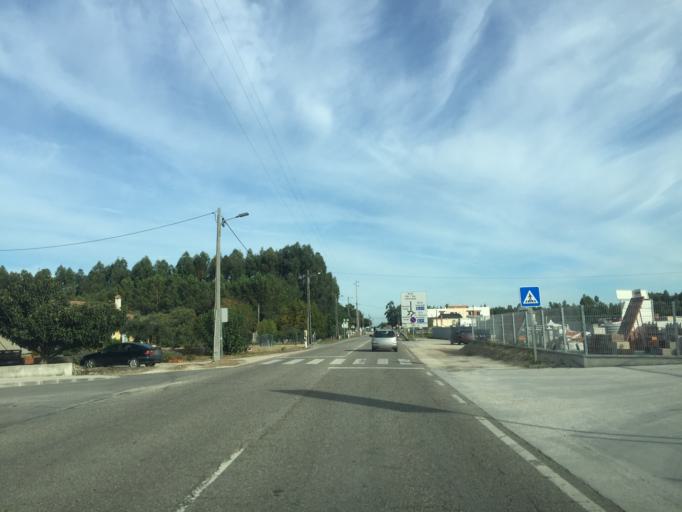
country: PT
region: Leiria
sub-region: Pombal
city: Lourical
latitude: 39.9880
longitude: -8.8013
